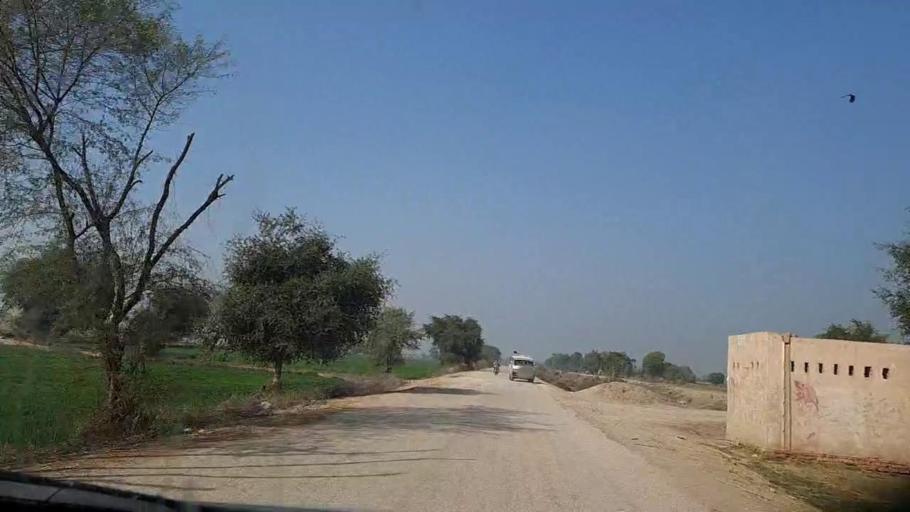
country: PK
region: Sindh
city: Moro
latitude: 26.7313
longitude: 67.9206
